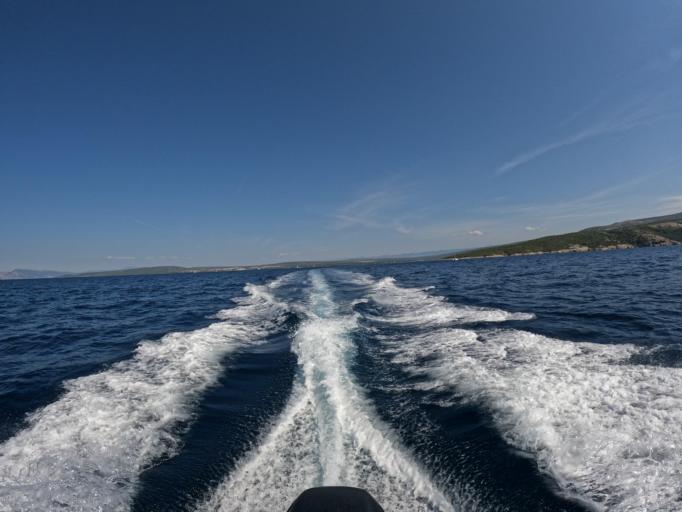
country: HR
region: Primorsko-Goranska
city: Punat
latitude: 44.9684
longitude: 14.6076
